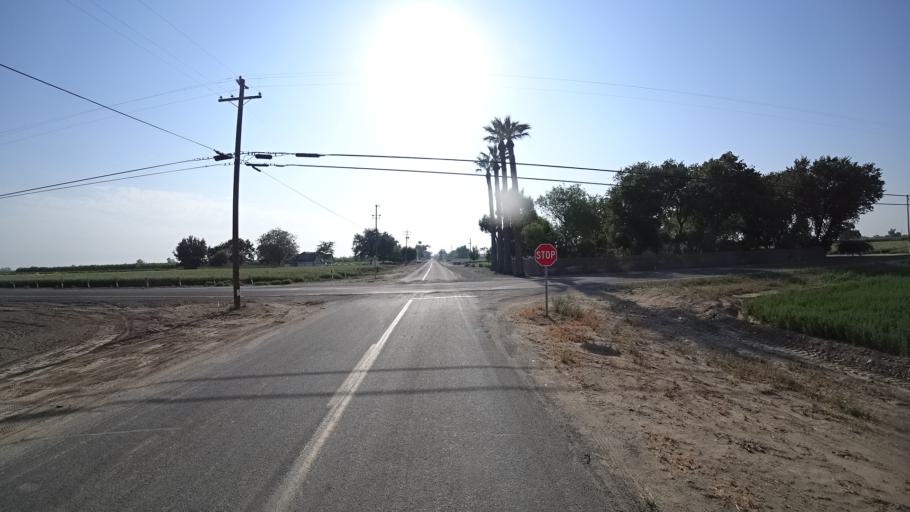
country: US
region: California
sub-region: Fresno County
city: Riverdale
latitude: 36.3583
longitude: -119.8516
